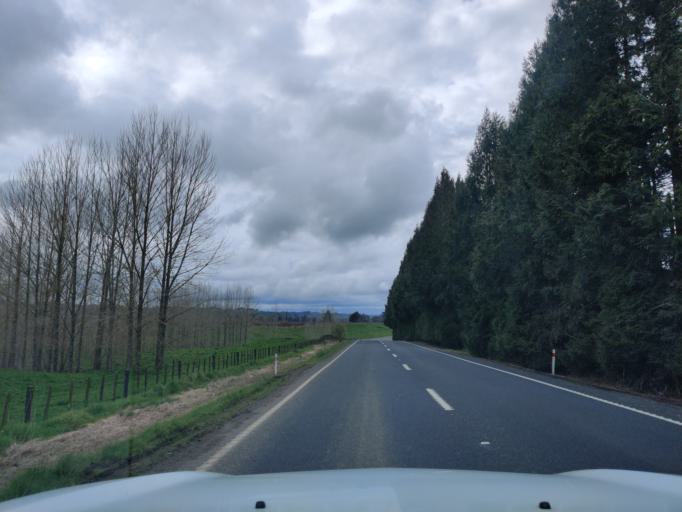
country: NZ
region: Waikato
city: Turangi
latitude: -39.0344
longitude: 175.3825
